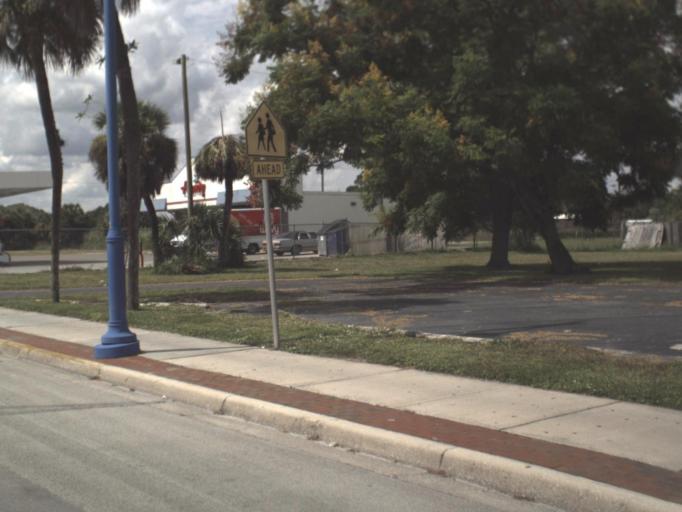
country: US
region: Florida
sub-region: Collier County
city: Immokalee
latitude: 26.4186
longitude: -81.4246
